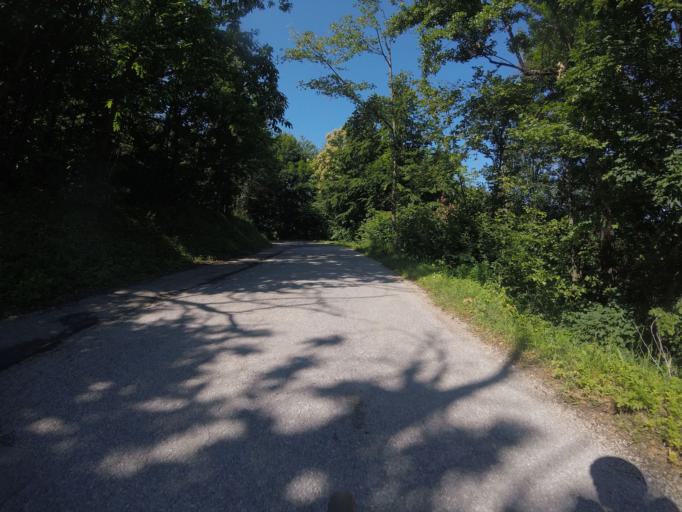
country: SI
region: Brezice
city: Brezice
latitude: 45.8240
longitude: 15.5481
